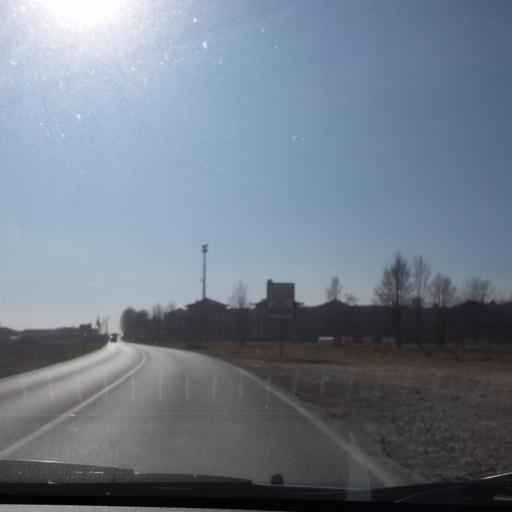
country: IT
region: Piedmont
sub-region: Provincia di Torino
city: Rivoli
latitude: 45.0661
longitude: 7.5314
